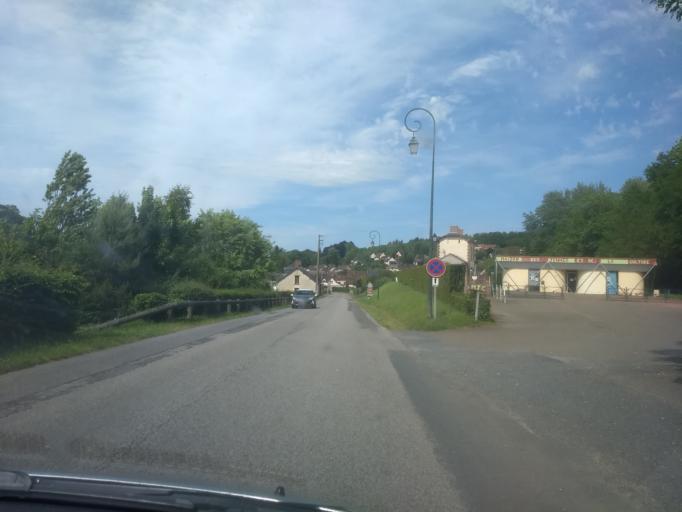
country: FR
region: Lower Normandy
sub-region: Departement de l'Orne
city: Longny-au-Perche
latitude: 48.5262
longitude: 0.7533
